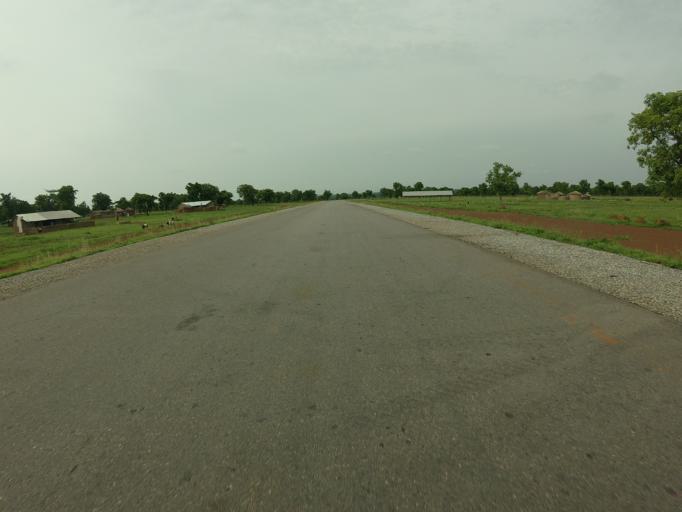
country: GH
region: Northern
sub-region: Yendi
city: Yendi
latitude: 9.8087
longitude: -0.1142
